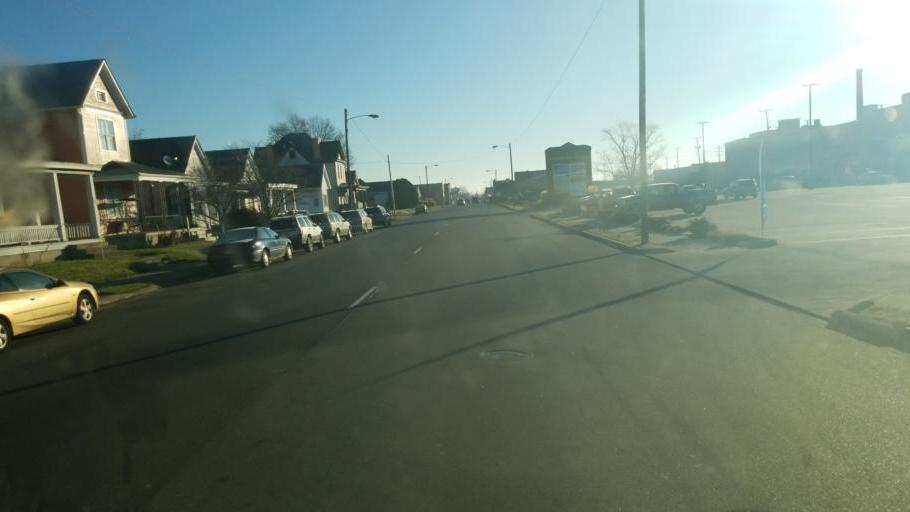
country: US
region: Ohio
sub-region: Scioto County
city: Portsmouth
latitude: 38.7389
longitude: -82.9817
